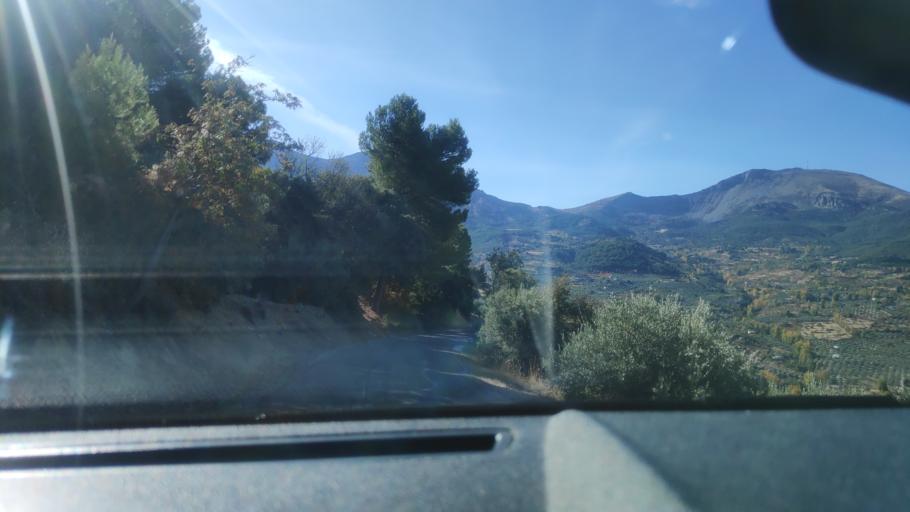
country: ES
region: Andalusia
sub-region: Provincia de Jaen
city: Torres
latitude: 37.7783
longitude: -3.4982
